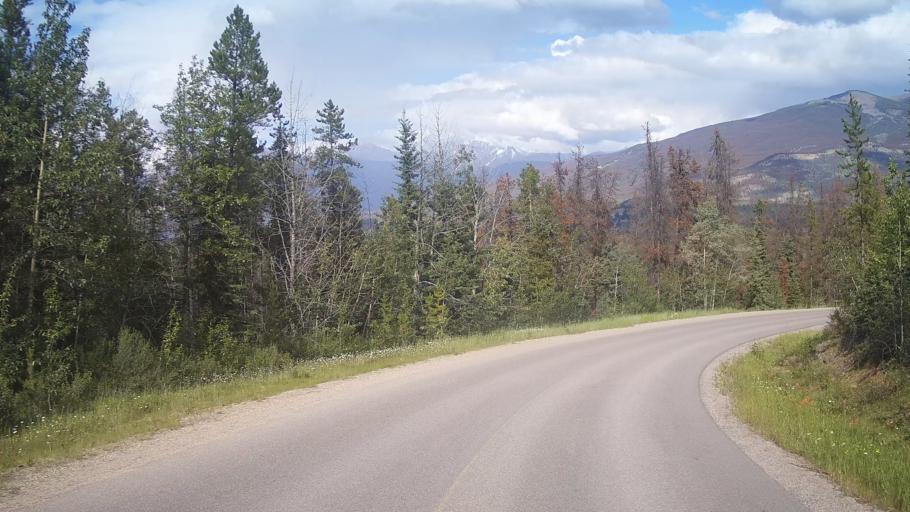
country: CA
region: Alberta
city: Jasper Park Lodge
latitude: 52.8590
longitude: -118.0996
